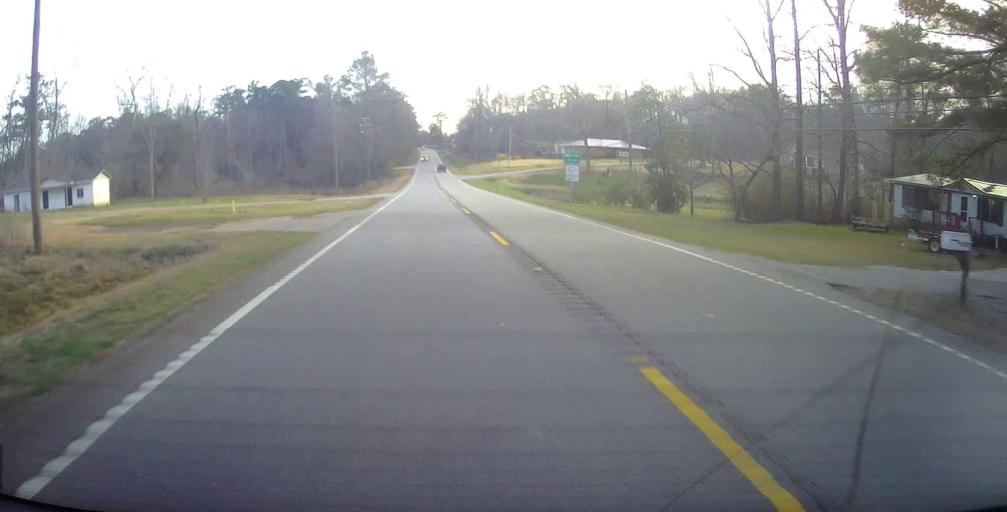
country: US
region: Georgia
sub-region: Troup County
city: West Point
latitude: 32.8964
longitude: -85.1641
